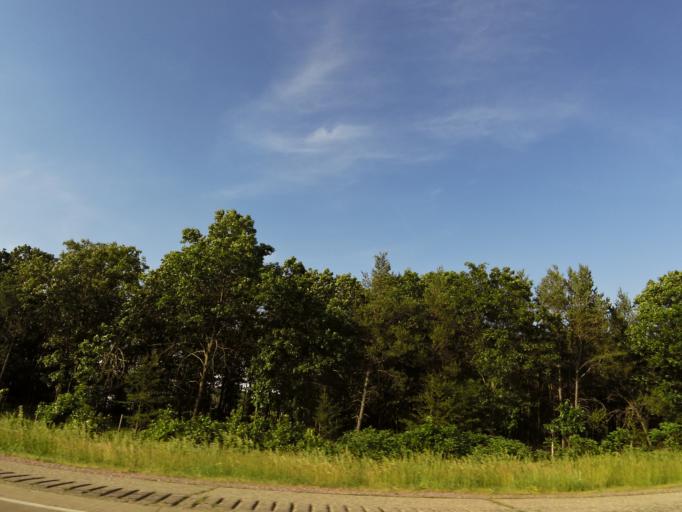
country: US
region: Wisconsin
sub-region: Columbia County
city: Wisconsin Dells
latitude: 43.7022
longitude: -89.8672
